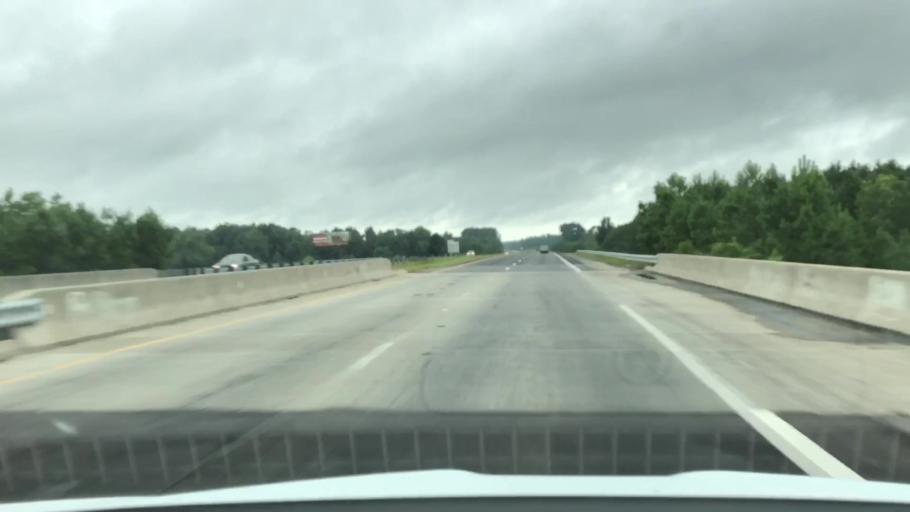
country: US
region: North Carolina
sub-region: Wayne County
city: Goldsboro
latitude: 35.4422
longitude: -77.9843
